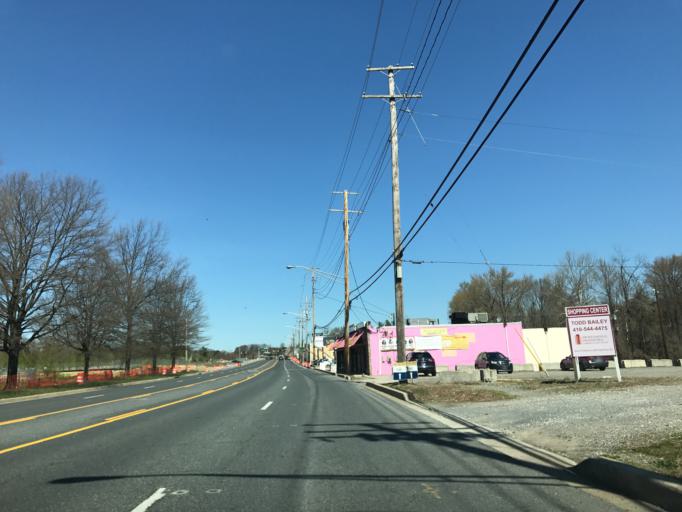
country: US
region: Maryland
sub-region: Anne Arundel County
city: Fort Meade
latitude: 39.1015
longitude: -76.7208
